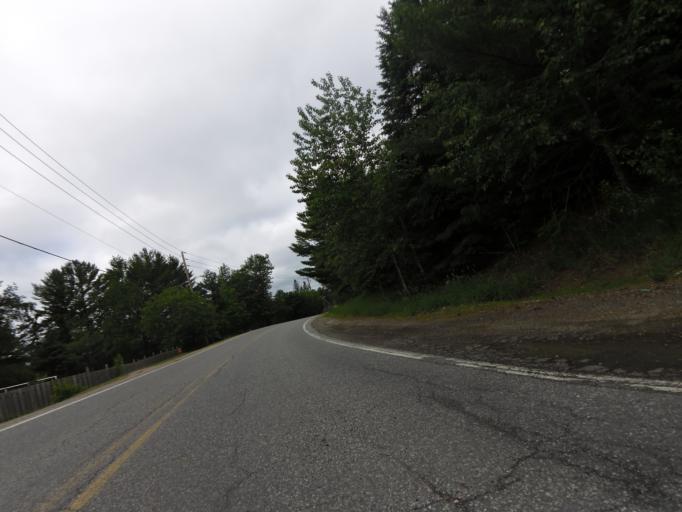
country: CA
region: Quebec
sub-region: Outaouais
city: Shawville
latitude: 45.8548
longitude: -76.4275
